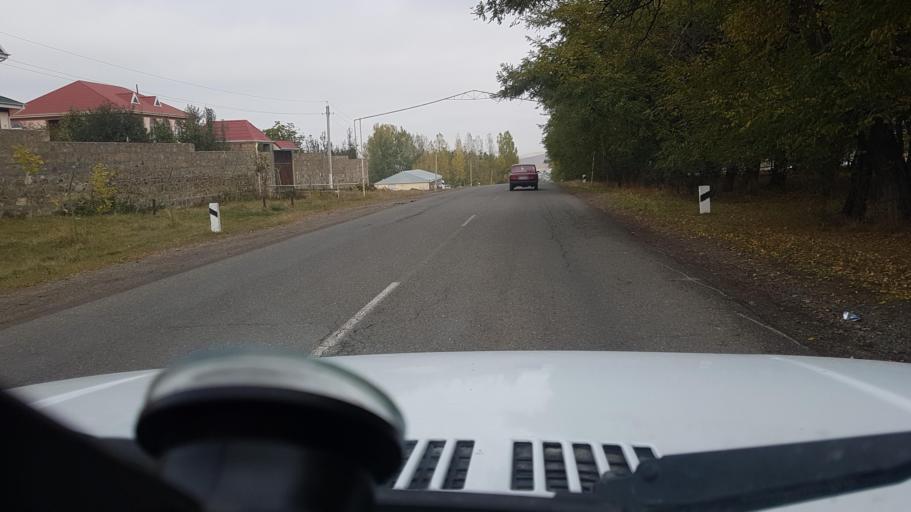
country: AZ
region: Gadabay Rayon
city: Ariqdam
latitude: 40.6205
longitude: 45.8131
